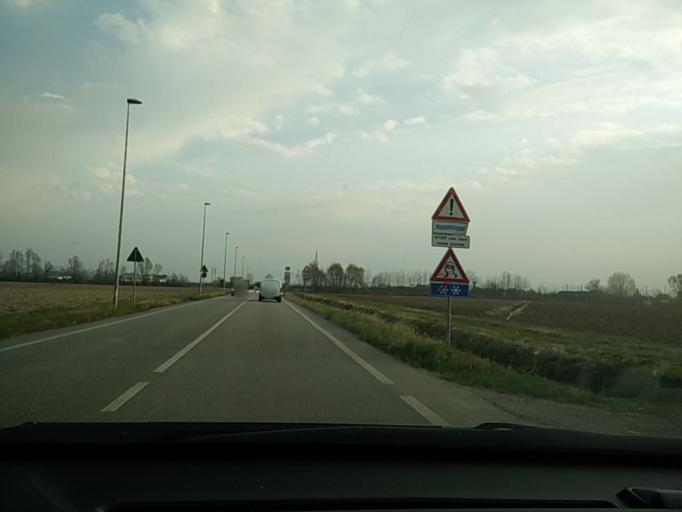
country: IT
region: Veneto
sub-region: Provincia di Venezia
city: Fossalta di Piave
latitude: 45.6274
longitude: 12.5044
